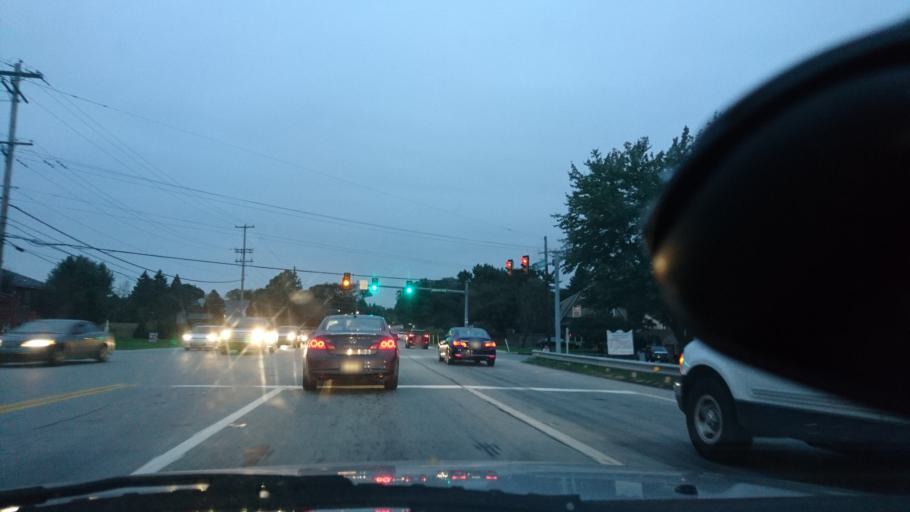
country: US
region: Pennsylvania
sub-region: Delaware County
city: Brookhaven
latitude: 39.8879
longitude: -75.4027
